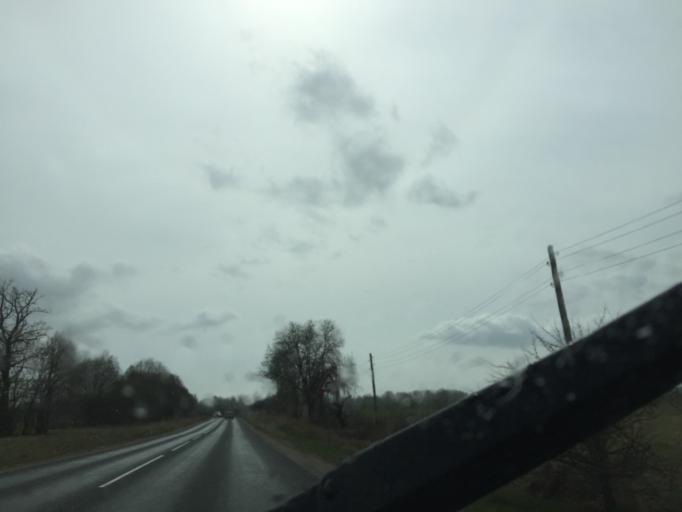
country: LV
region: Priekuli
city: Priekuli
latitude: 57.3404
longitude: 25.3349
